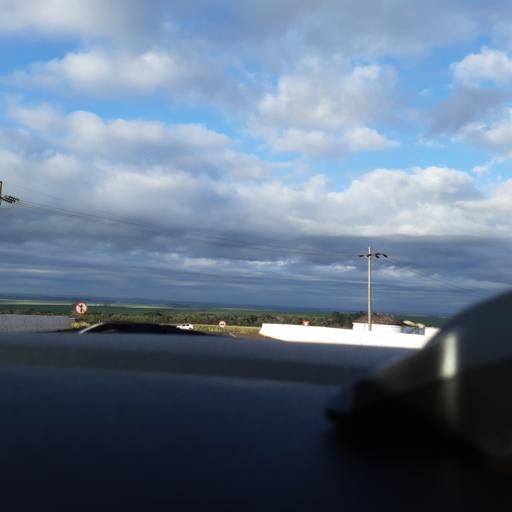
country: BR
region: Sao Paulo
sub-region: Ourinhos
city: Ourinhos
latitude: -22.9941
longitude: -49.8459
